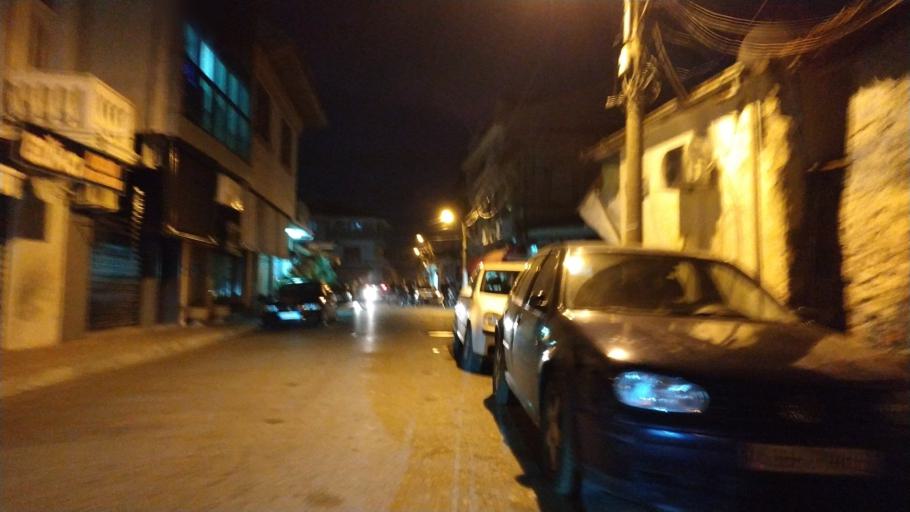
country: AL
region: Shkoder
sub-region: Rrethi i Shkodres
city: Shkoder
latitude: 42.0664
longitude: 19.5072
